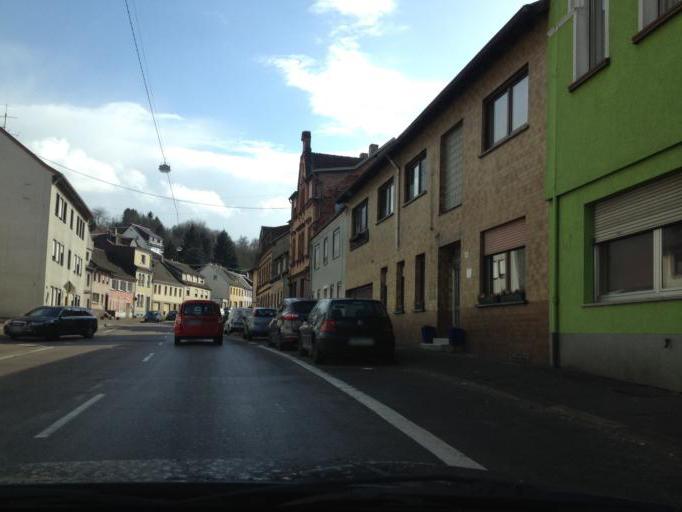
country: DE
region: Saarland
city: Neunkirchen
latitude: 49.3654
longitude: 7.1850
